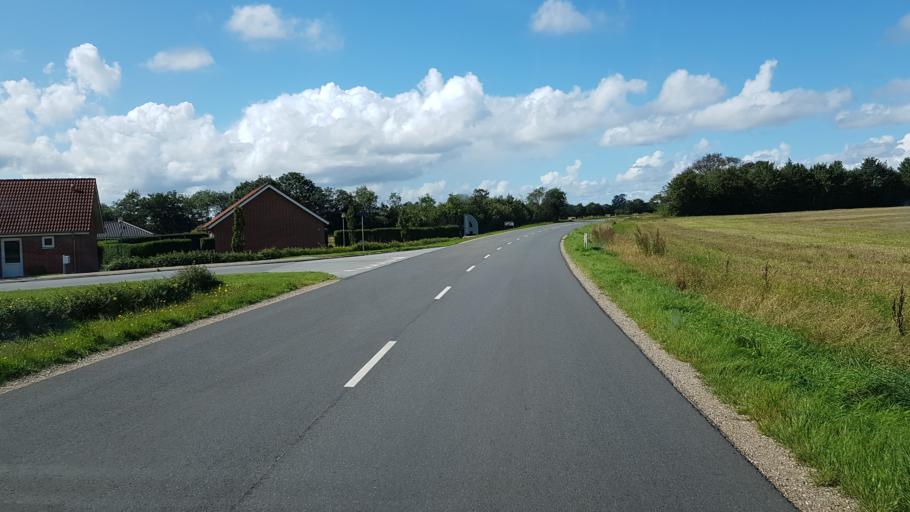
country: DK
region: South Denmark
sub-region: Vejen Kommune
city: Holsted
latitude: 55.6044
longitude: 8.7908
